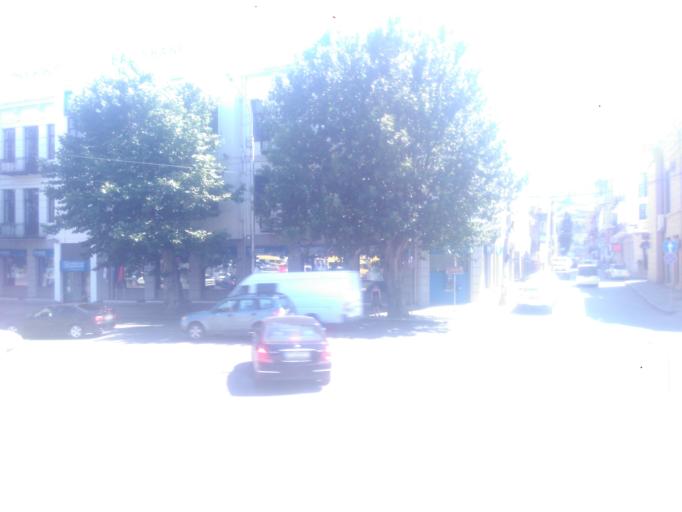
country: GE
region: T'bilisi
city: Tbilisi
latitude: 41.6921
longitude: 44.8146
